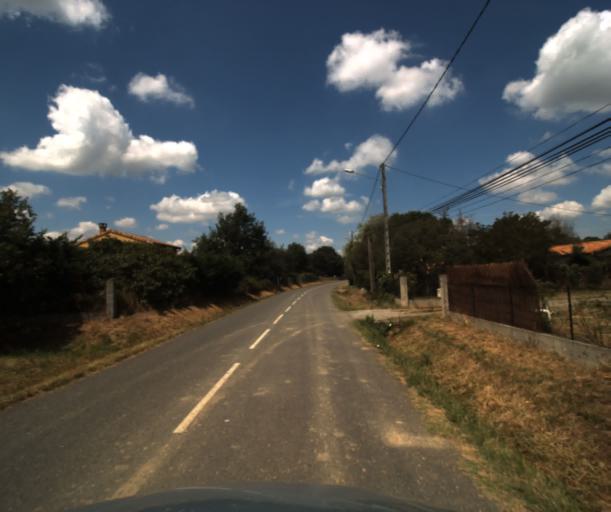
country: FR
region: Midi-Pyrenees
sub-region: Departement de la Haute-Garonne
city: Labastidette
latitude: 43.4646
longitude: 1.2115
